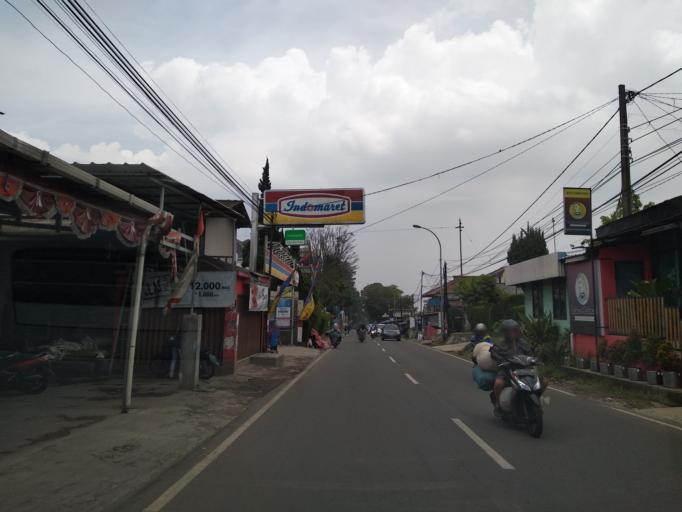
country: ID
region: West Java
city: Lembang
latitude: -6.8304
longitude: 107.6066
